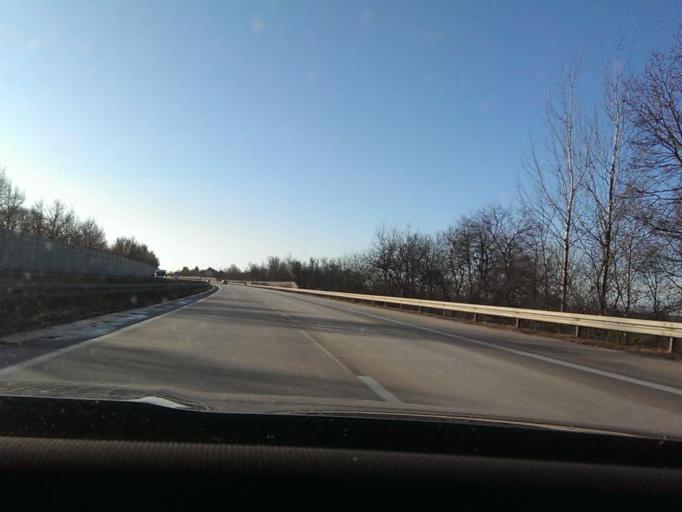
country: DE
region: Lower Saxony
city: Langenhagen
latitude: 52.4800
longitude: 9.7200
